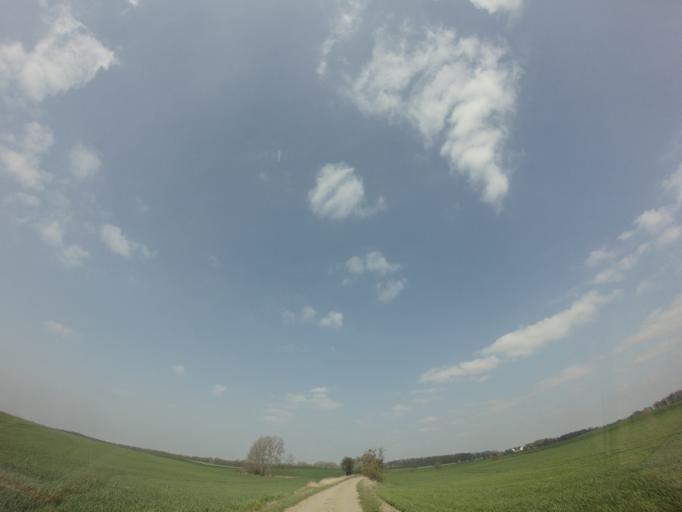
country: PL
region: West Pomeranian Voivodeship
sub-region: Powiat choszczenski
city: Pelczyce
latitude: 53.0846
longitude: 15.3452
